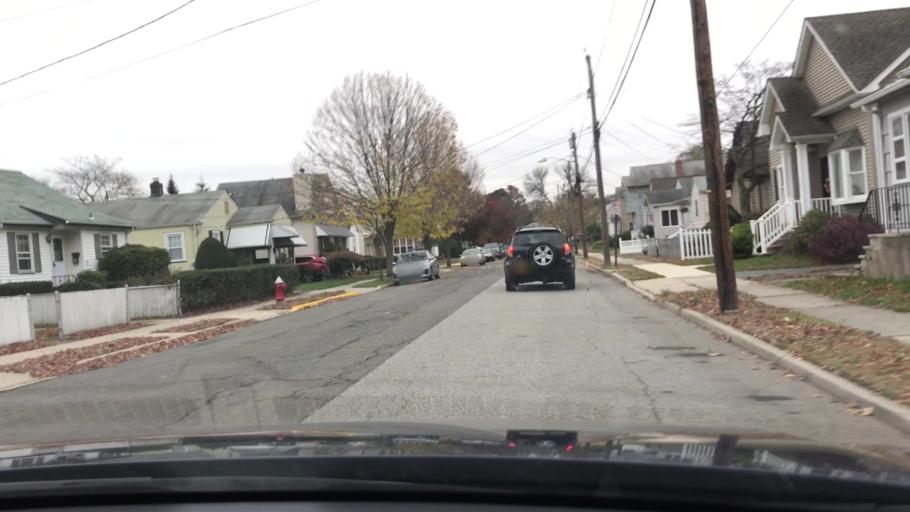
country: US
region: New Jersey
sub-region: Bergen County
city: Wallington
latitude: 40.8470
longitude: -74.1163
